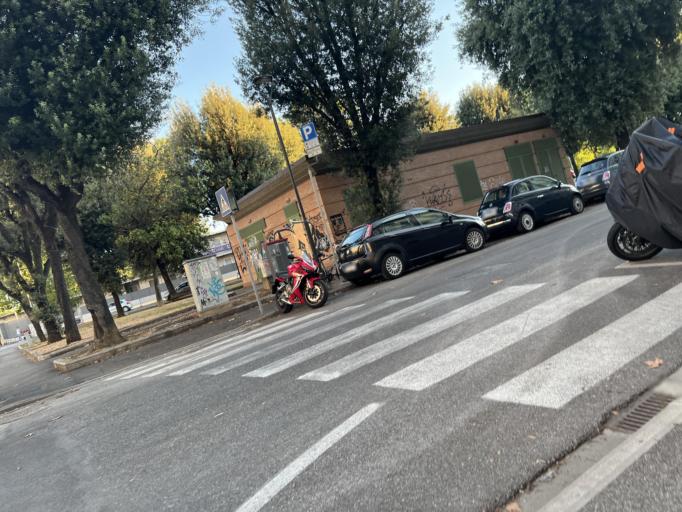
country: IT
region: Tuscany
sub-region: Province of Florence
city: Florence
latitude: 43.7847
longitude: 11.2511
